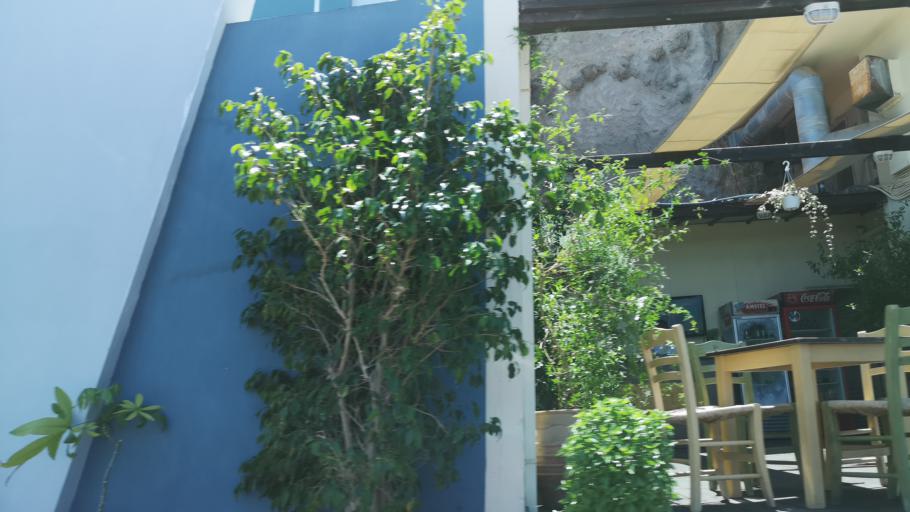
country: GR
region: Crete
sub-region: Nomos Lasithiou
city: Agios Nikolaos
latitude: 35.1905
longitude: 25.7219
